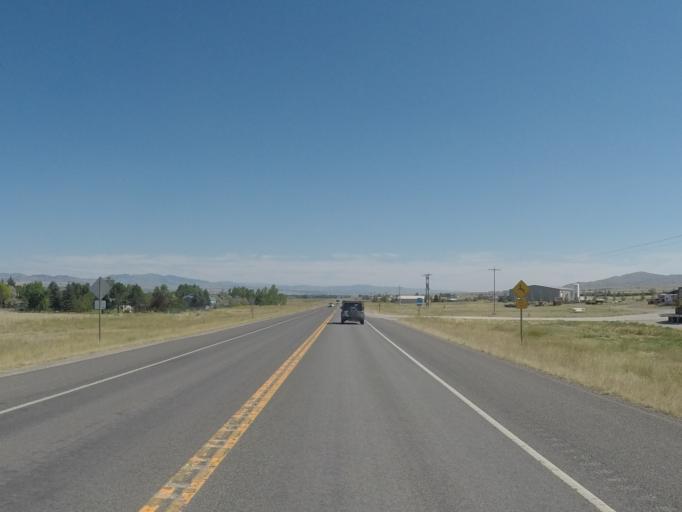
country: US
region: Montana
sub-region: Broadwater County
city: Townsend
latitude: 46.3905
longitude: -111.5767
